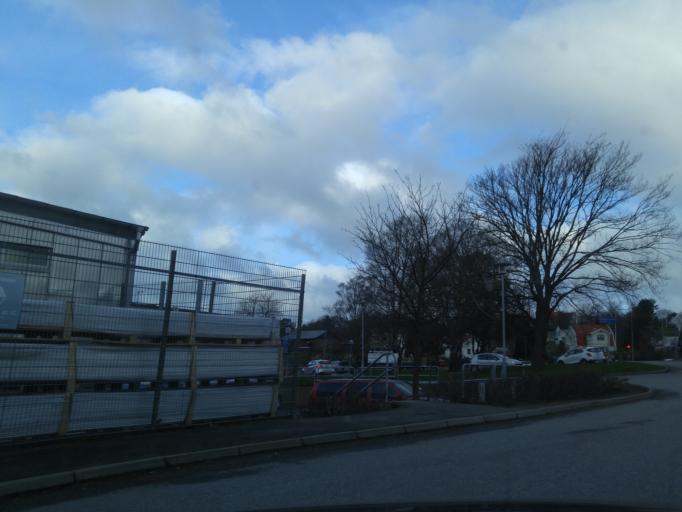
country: SE
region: Vaestra Goetaland
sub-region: Goteborg
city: Majorna
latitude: 57.6709
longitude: 11.8803
